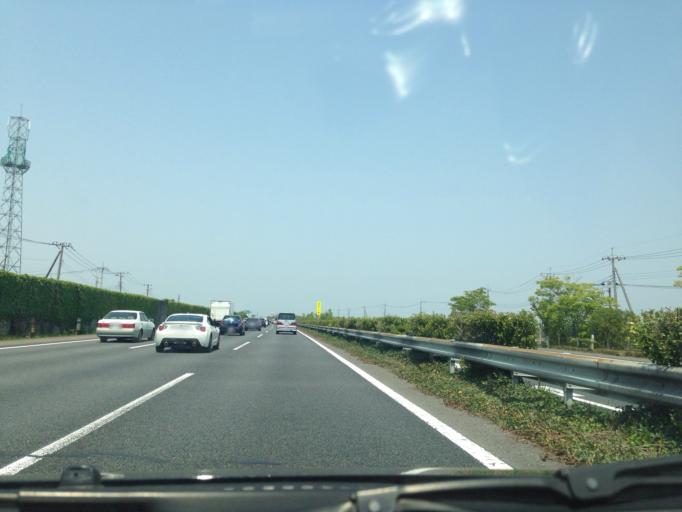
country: JP
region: Saitama
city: Hanyu
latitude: 36.1942
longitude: 139.5820
